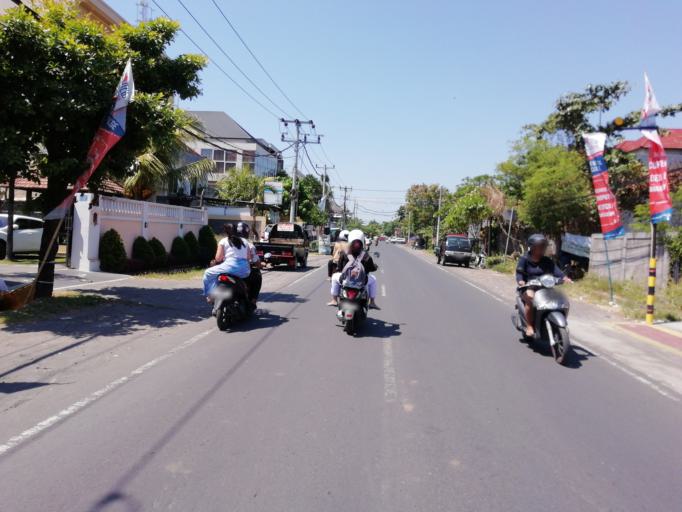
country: ID
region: Bali
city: Karyadharma
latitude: -8.6844
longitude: 115.2314
